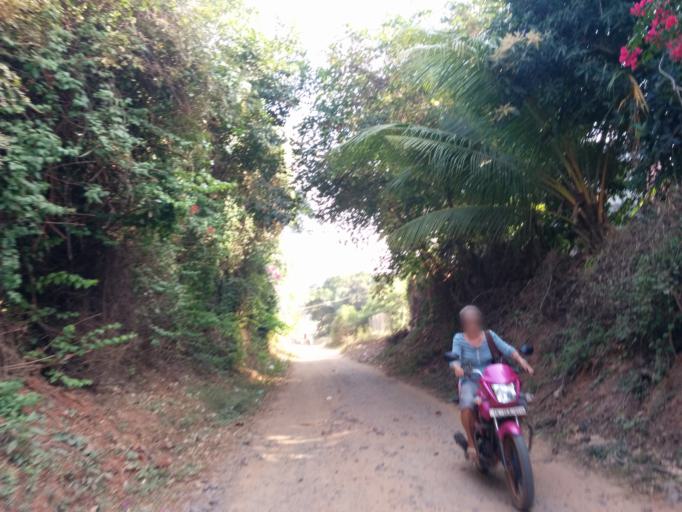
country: IN
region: Tamil Nadu
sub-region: Villupuram
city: Auroville
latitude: 11.9845
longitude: 79.8335
